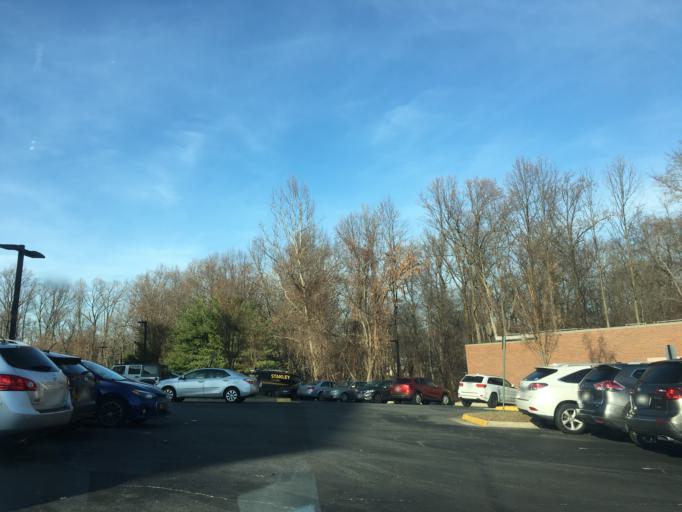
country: US
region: Virginia
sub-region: City of Fairfax
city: Fairfax
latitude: 38.8616
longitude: -77.3016
